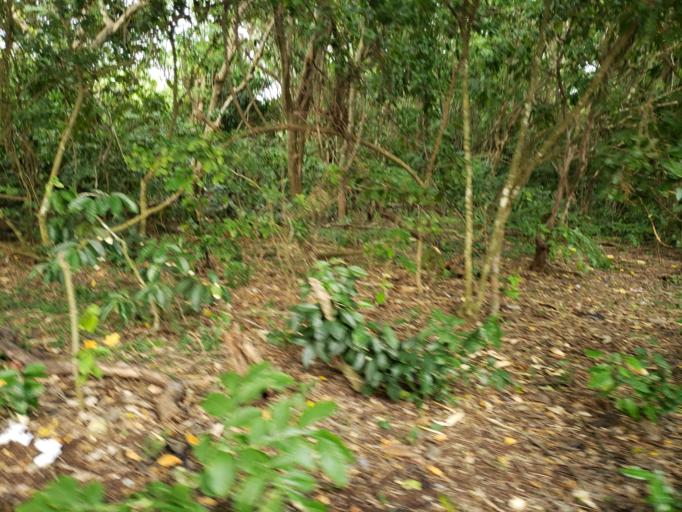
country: ID
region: Bali
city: Pecatu
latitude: -8.8315
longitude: 115.0856
